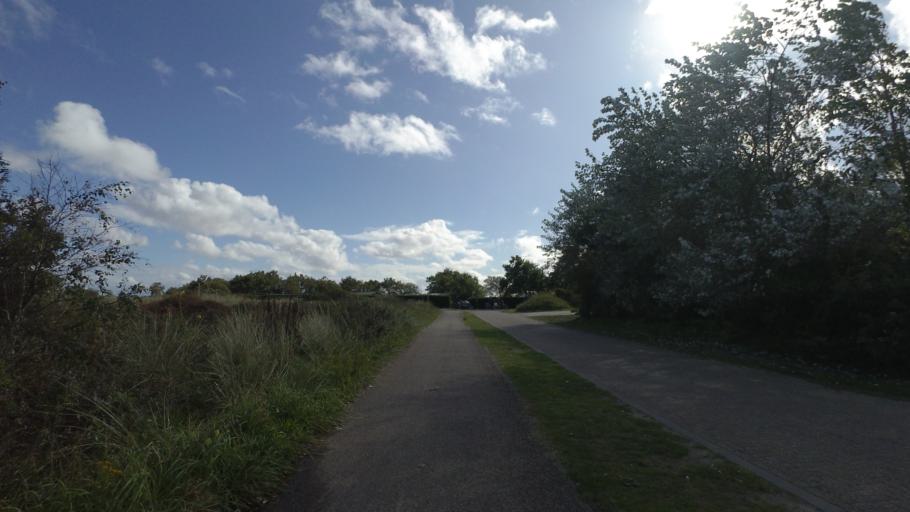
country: NL
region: Friesland
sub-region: Gemeente Ameland
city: Nes
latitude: 53.4542
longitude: 5.8142
